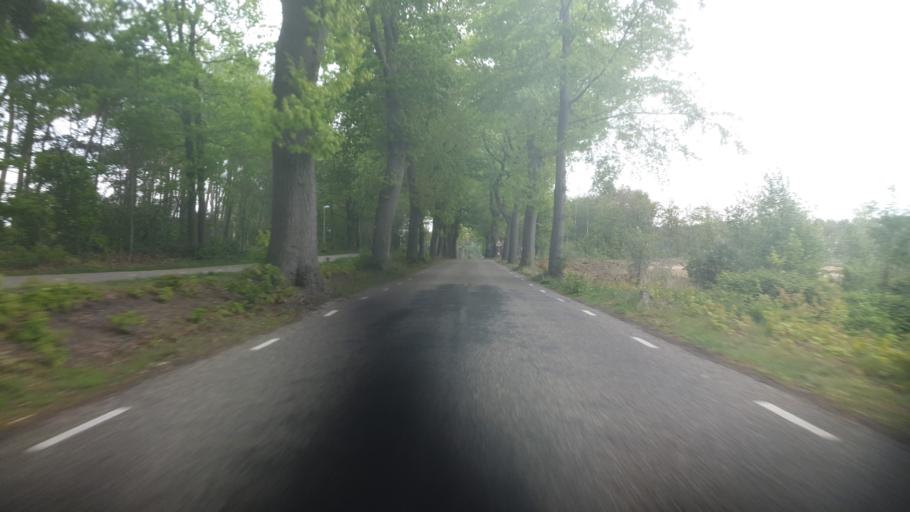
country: NL
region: Gelderland
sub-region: Gemeente Nijmegen
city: Lindenholt
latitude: 51.7845
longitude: 5.8011
